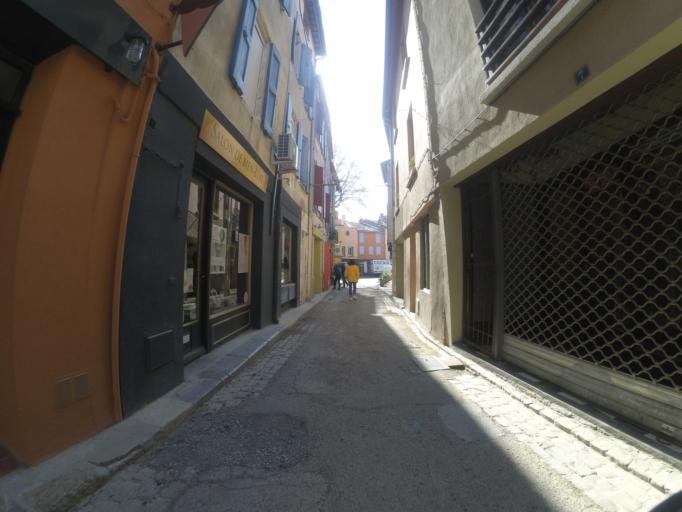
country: FR
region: Languedoc-Roussillon
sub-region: Departement des Pyrenees-Orientales
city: Thuir
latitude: 42.6338
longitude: 2.7556
